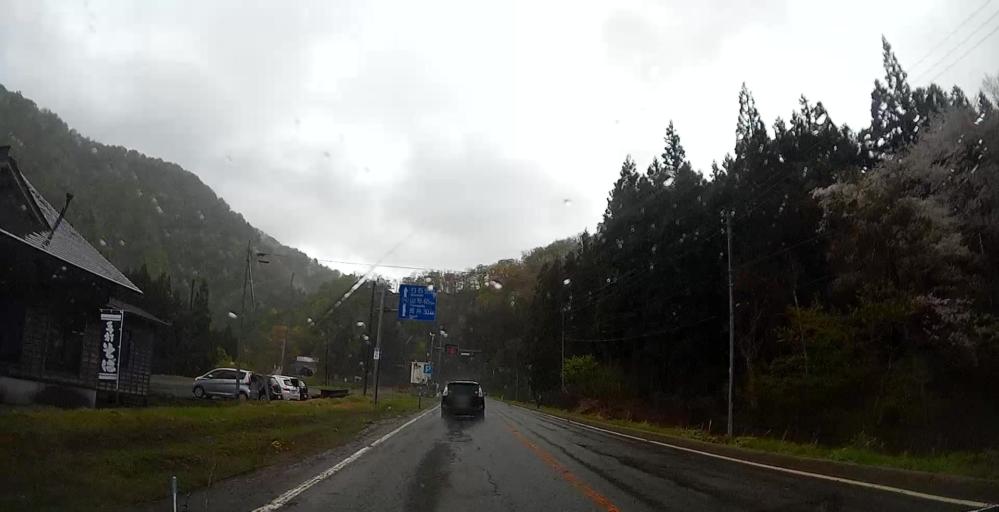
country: JP
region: Yamagata
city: Nagai
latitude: 38.0485
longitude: 139.8419
